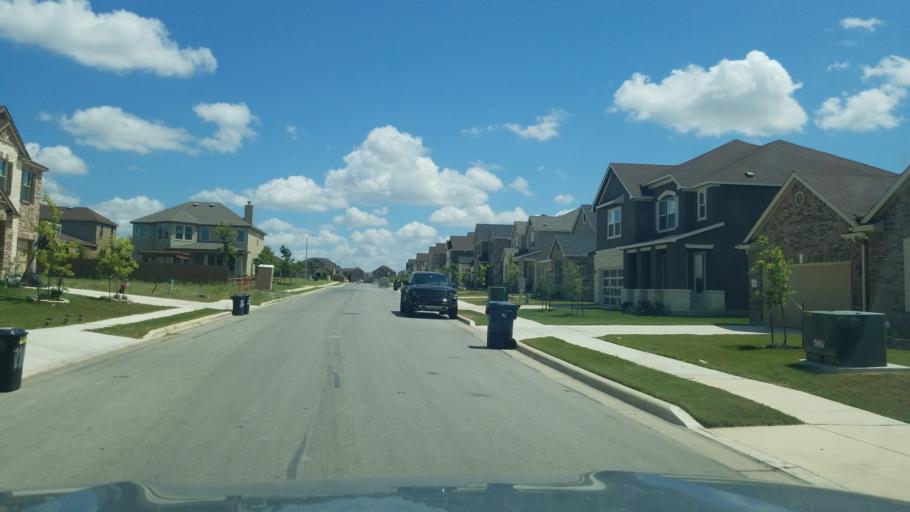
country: US
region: Texas
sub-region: Bexar County
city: Converse
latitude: 29.5379
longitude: -98.3245
